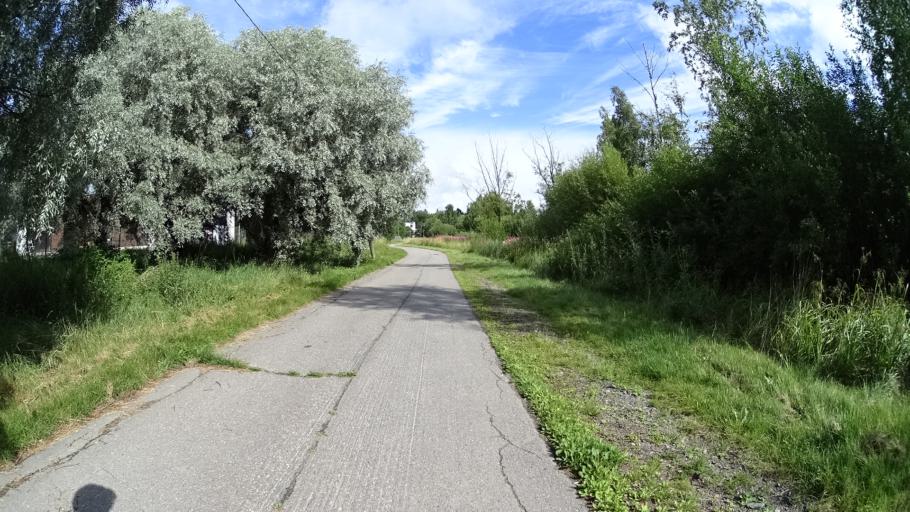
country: FI
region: Uusimaa
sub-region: Helsinki
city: Kilo
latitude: 60.2068
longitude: 24.7607
